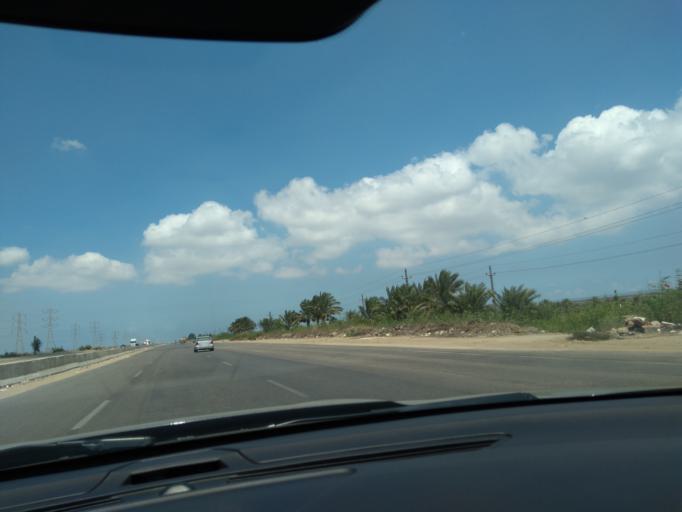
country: EG
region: Muhafazat Bur Sa`id
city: Port Said
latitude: 31.1623
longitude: 32.3018
